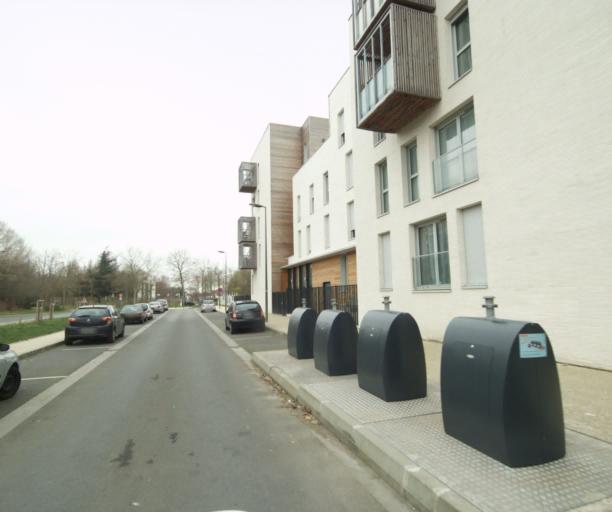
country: FR
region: Ile-de-France
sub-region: Departement du Val-d'Oise
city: Vaureal
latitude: 49.0439
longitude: 2.0278
